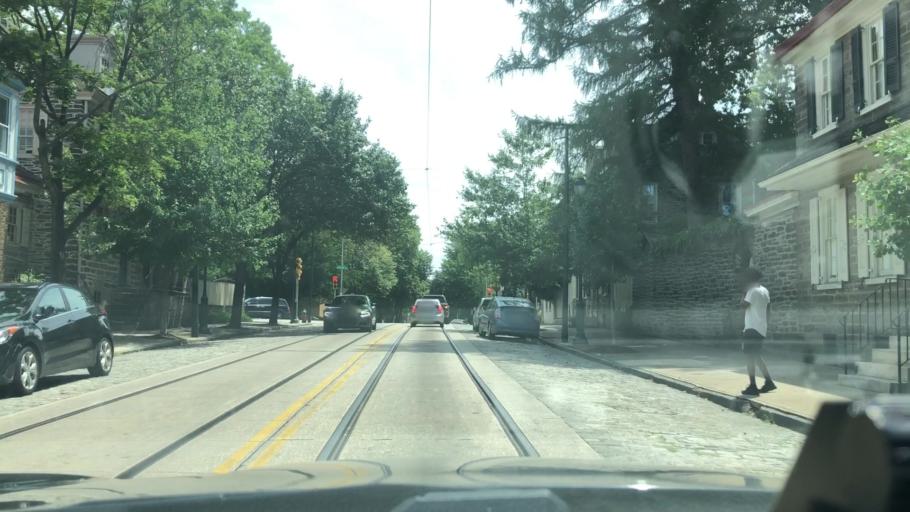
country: US
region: Pennsylvania
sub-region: Montgomery County
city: Wyndmoor
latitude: 40.0490
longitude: -75.1838
